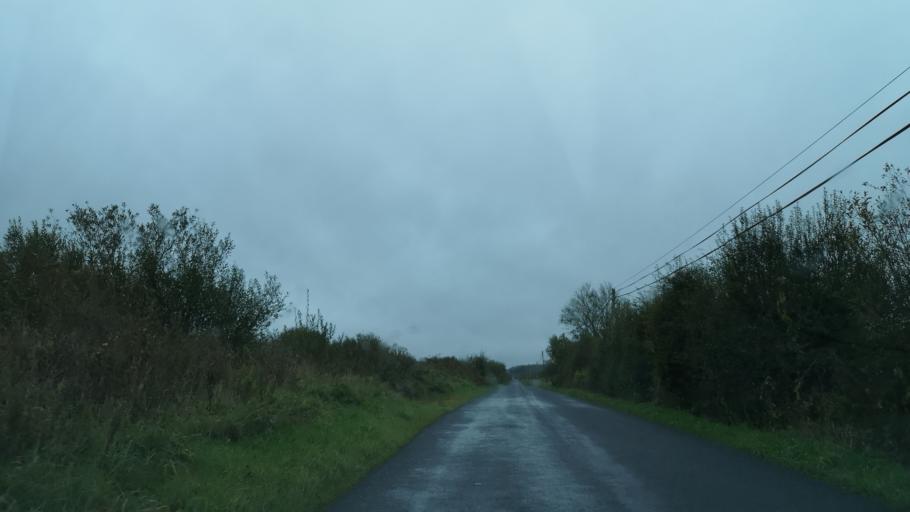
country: IE
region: Connaught
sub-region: Roscommon
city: Ballaghaderreen
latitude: 53.8948
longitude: -8.5752
